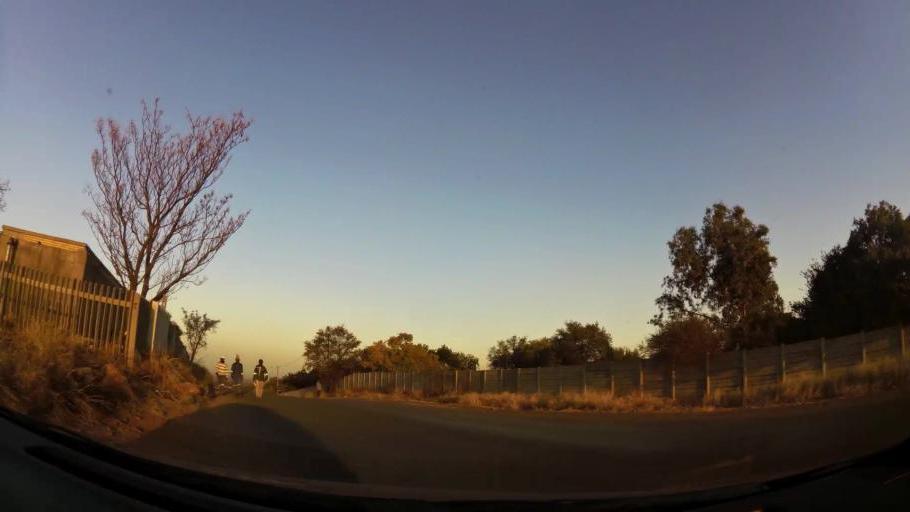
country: ZA
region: North-West
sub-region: Bojanala Platinum District Municipality
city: Rustenburg
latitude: -25.6309
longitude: 27.2039
